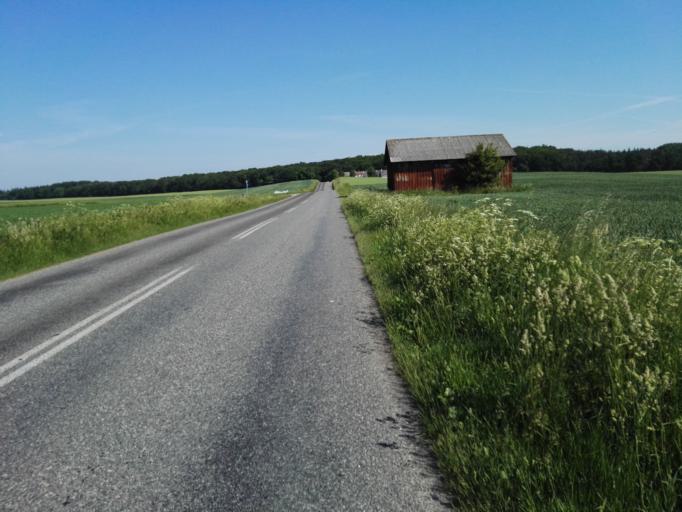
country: DK
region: Zealand
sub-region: Lejre Kommune
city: Ejby
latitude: 55.7246
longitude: 11.8879
